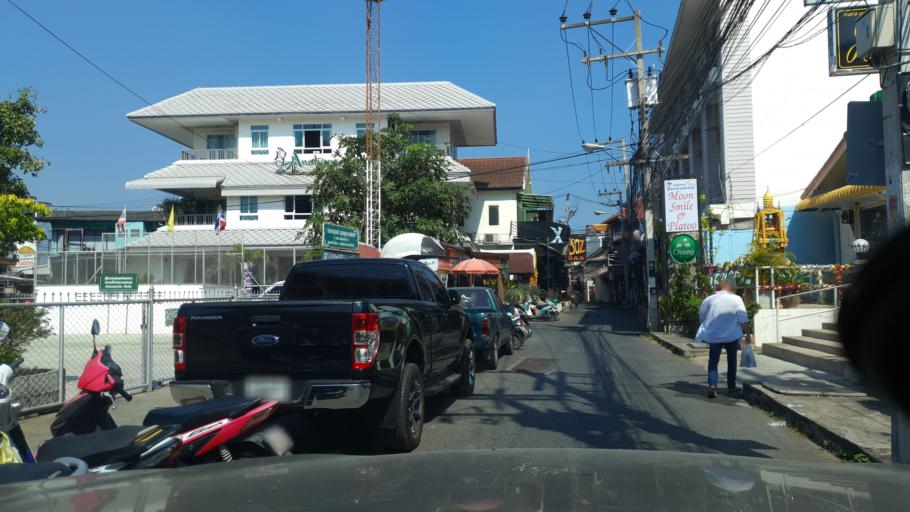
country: TH
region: Prachuap Khiri Khan
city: Hua Hin
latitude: 12.5707
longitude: 99.9586
